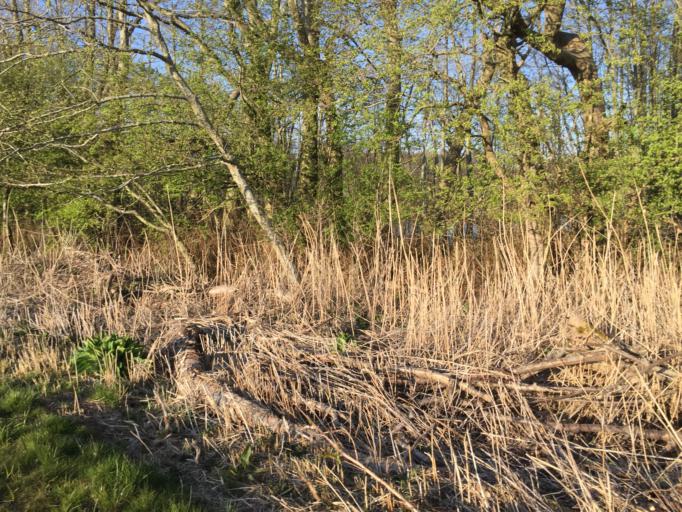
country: DK
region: South Denmark
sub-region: Odense Kommune
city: Hojby
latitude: 55.3529
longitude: 10.4323
